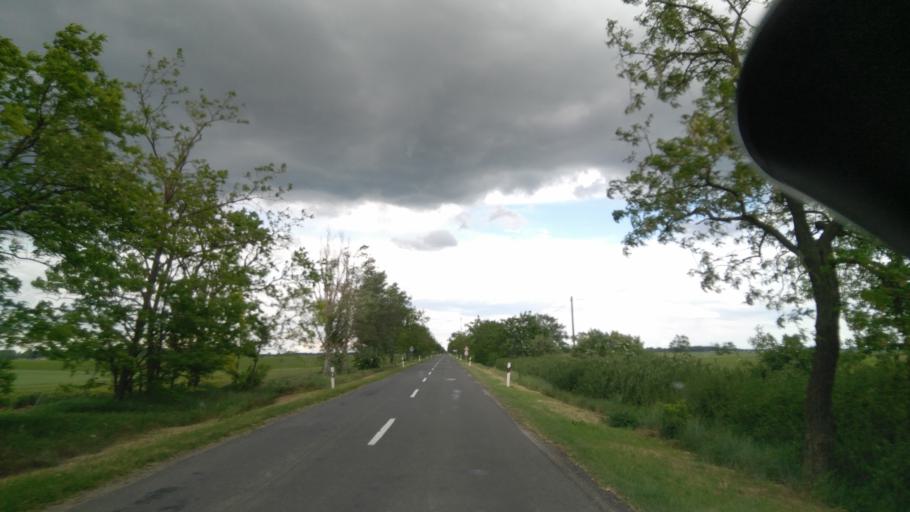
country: HU
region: Bekes
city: Gadoros
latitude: 46.6720
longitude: 20.6255
